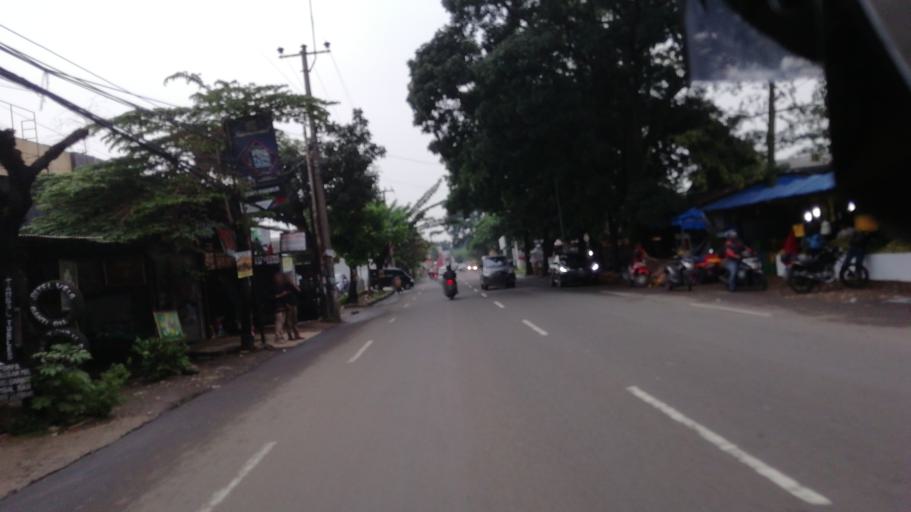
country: ID
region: West Java
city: Cibinong
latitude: -6.5118
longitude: 106.8070
